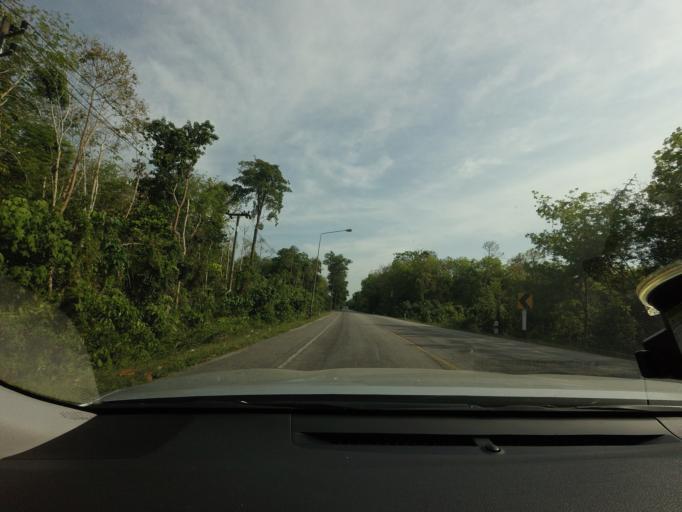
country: TH
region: Narathiwat
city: Narathiwat
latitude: 6.3546
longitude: 101.7909
